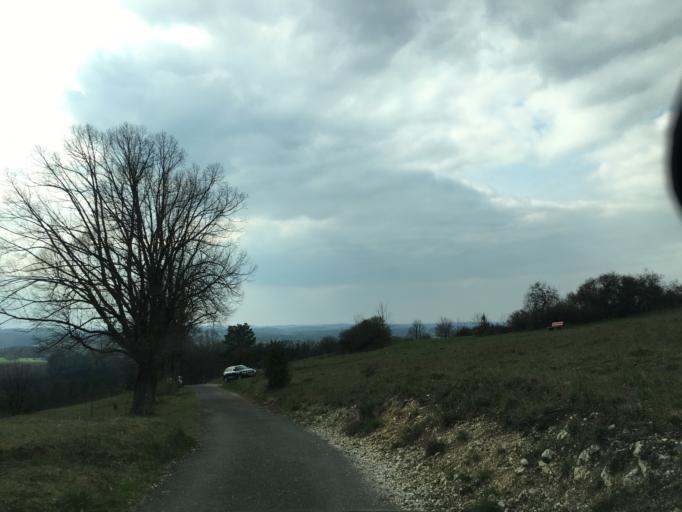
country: DE
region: Bavaria
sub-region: Upper Franconia
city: Pottenstein
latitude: 49.7661
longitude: 11.4171
